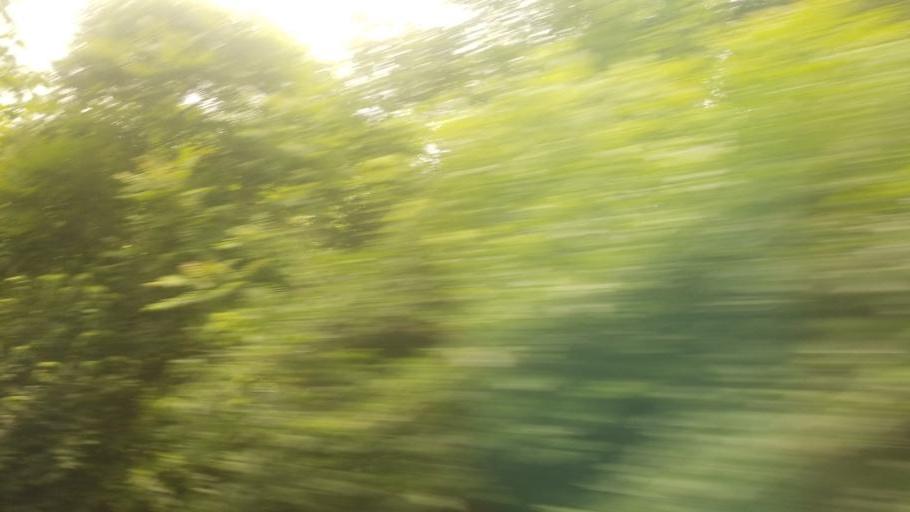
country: US
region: Maryland
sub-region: Montgomery County
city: Poolesville
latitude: 39.2059
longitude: -77.3675
